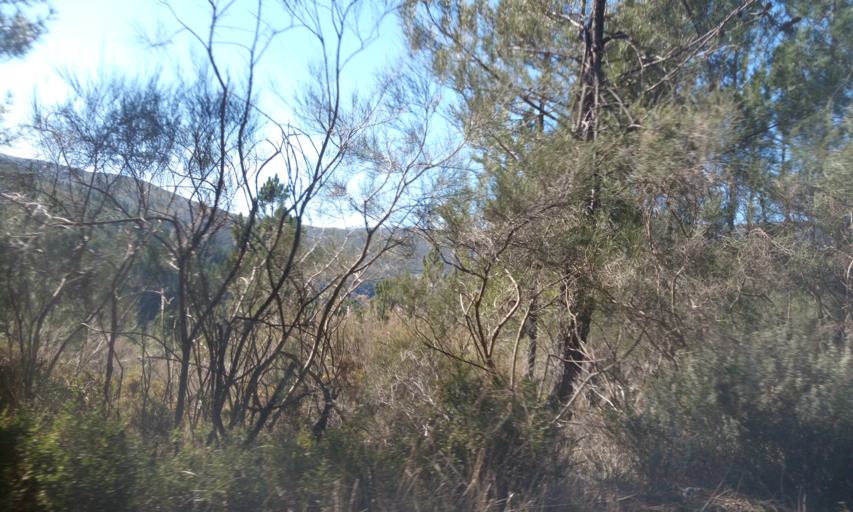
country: PT
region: Guarda
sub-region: Manteigas
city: Manteigas
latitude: 40.4442
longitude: -7.5072
